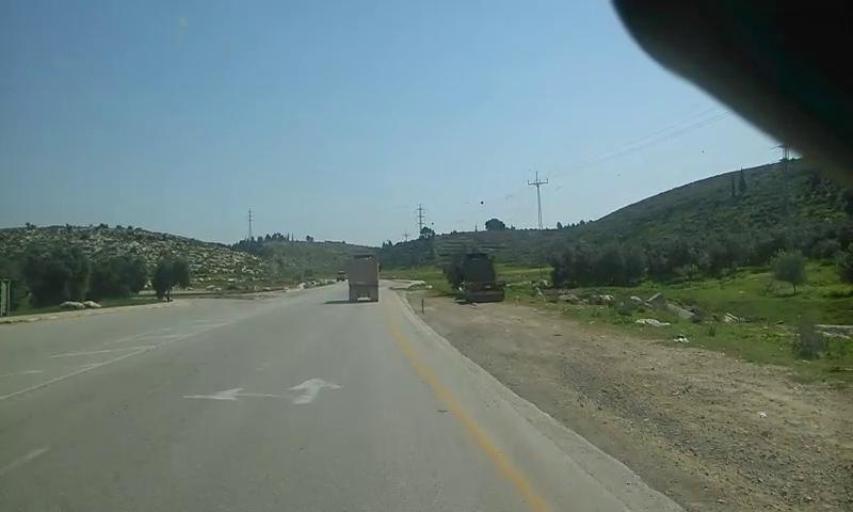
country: PS
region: West Bank
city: Idhna
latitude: 31.5841
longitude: 34.9734
